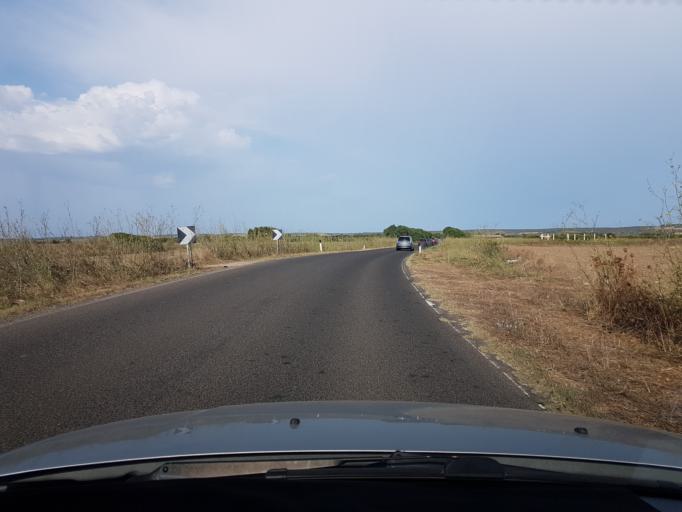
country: IT
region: Sardinia
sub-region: Provincia di Oristano
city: Cabras
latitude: 39.9163
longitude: 8.4814
